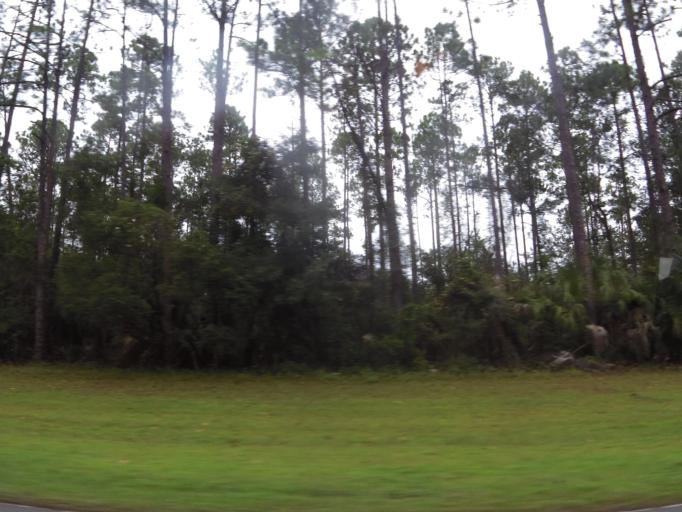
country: US
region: Florida
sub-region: Duval County
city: Baldwin
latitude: 30.2256
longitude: -81.8918
